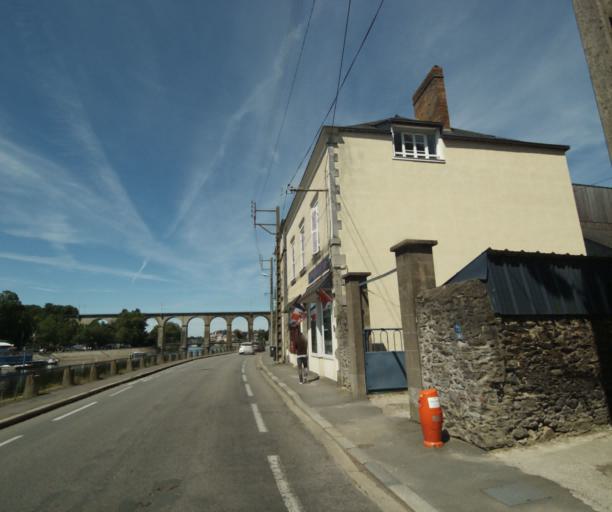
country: FR
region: Pays de la Loire
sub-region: Departement de la Mayenne
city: Laval
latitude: 48.0743
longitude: -0.7704
